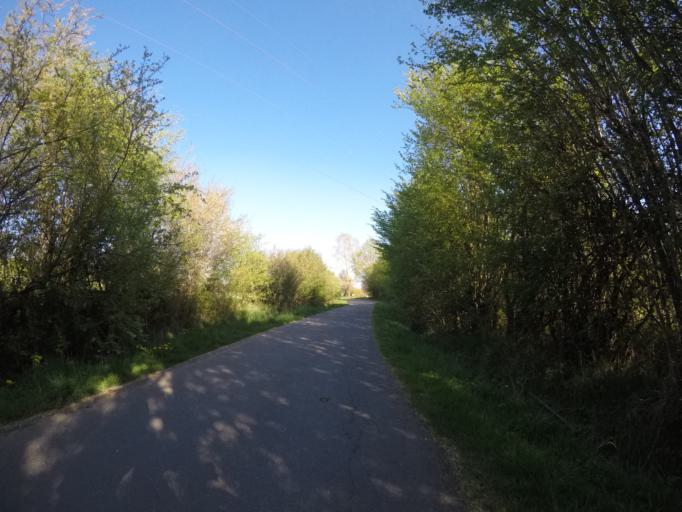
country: BE
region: Wallonia
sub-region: Province du Luxembourg
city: Tintigny
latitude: 49.7170
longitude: 5.5508
